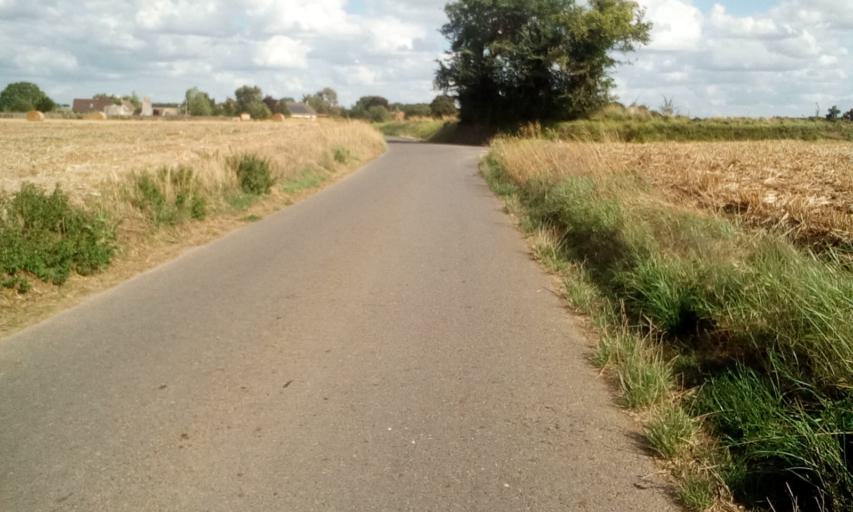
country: FR
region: Lower Normandy
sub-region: Departement du Calvados
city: Saint-Sylvain
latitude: 49.0882
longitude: -0.2044
